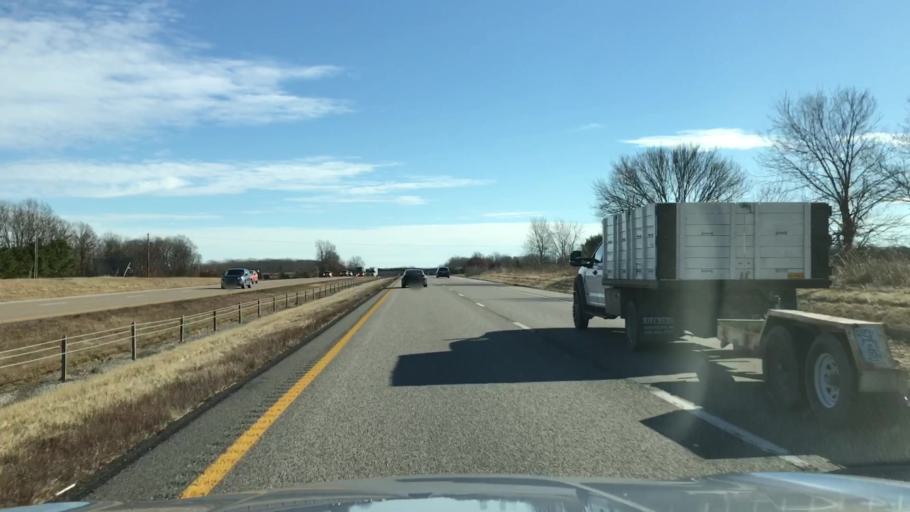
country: US
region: Missouri
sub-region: Montgomery County
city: Montgomery City
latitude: 38.8998
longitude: -91.6366
